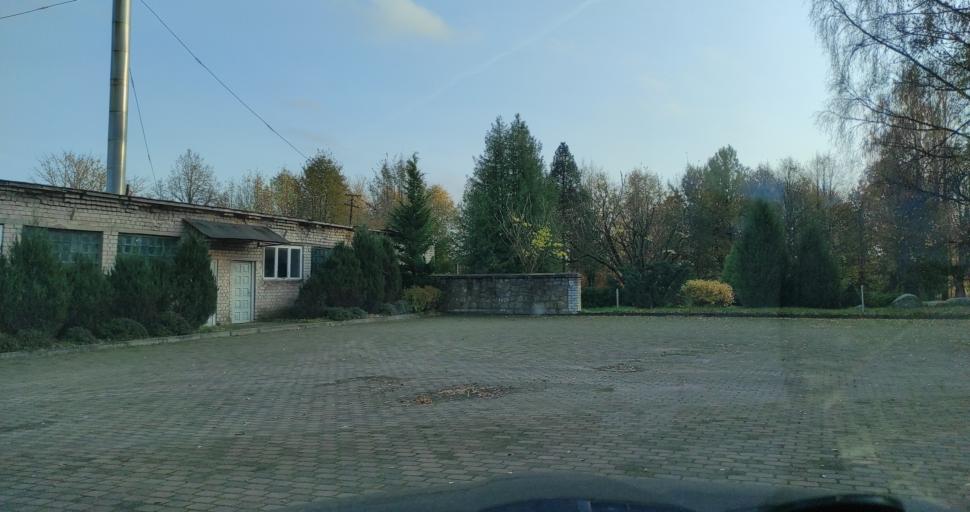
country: LV
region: Vainode
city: Vainode
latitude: 56.4355
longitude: 21.8754
